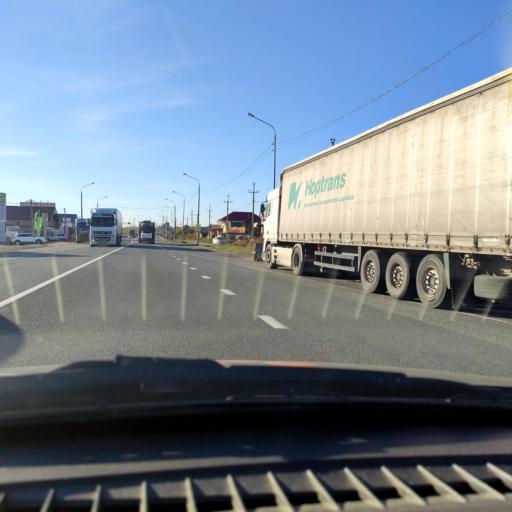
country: RU
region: Samara
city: Mezhdurechensk
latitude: 53.2483
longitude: 49.1730
